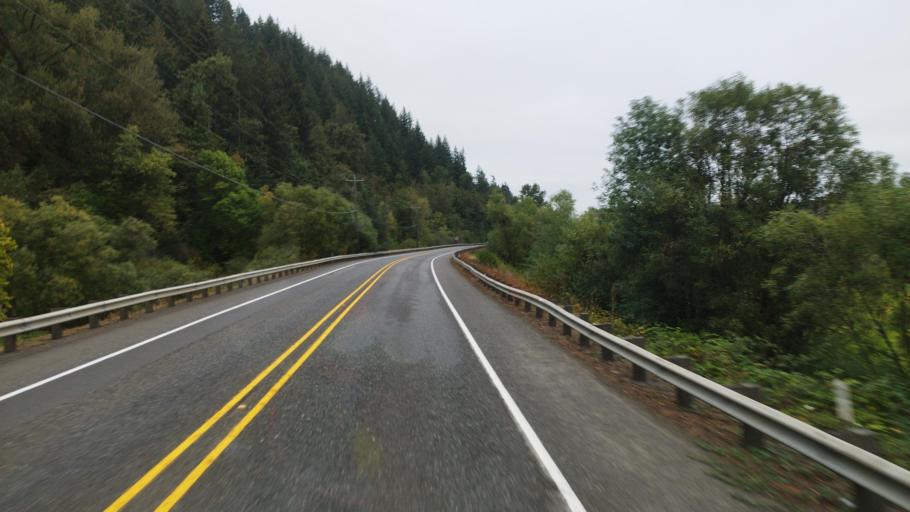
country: US
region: Oregon
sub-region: Columbia County
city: Rainier
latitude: 46.0498
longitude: -122.8983
